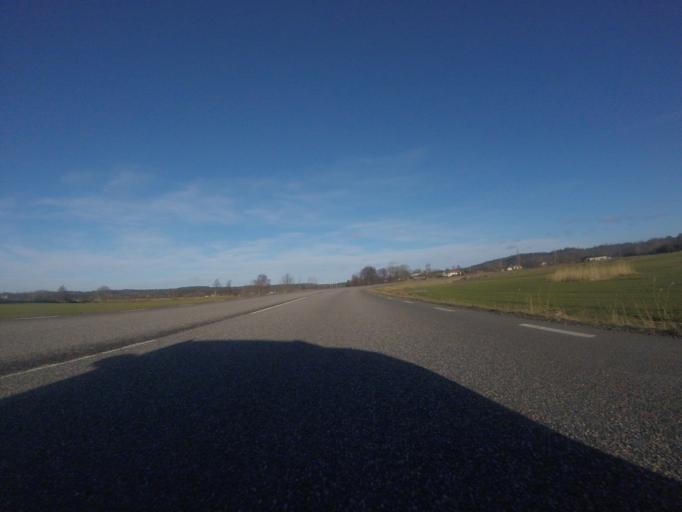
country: SE
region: Halland
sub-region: Varbergs Kommun
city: Veddige
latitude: 57.2182
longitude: 12.2278
